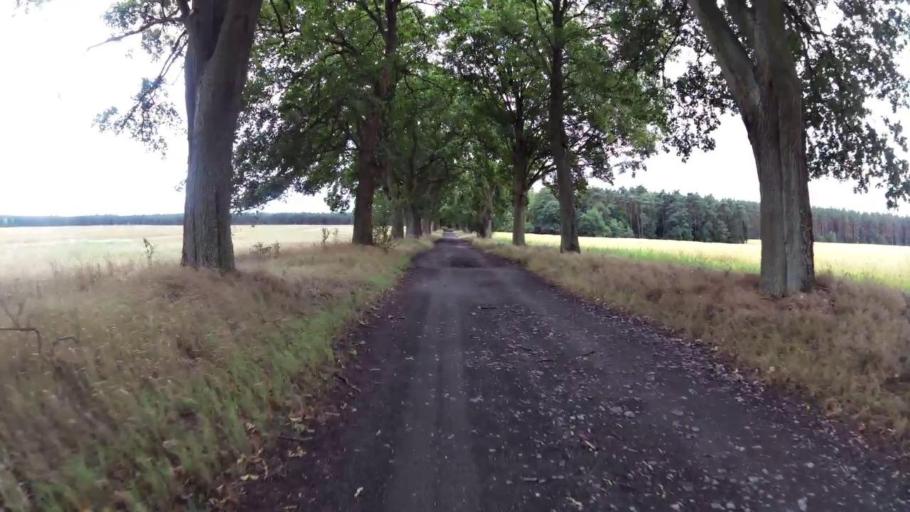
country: PL
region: West Pomeranian Voivodeship
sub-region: Powiat mysliborski
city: Debno
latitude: 52.8728
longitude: 14.7130
